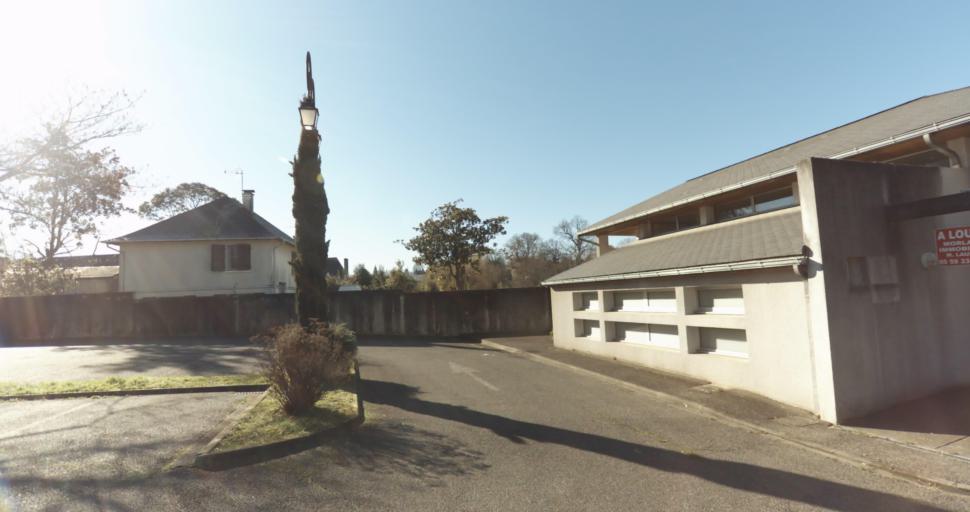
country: FR
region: Aquitaine
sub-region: Departement des Pyrenees-Atlantiques
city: Morlaas
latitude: 43.3445
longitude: -0.2646
